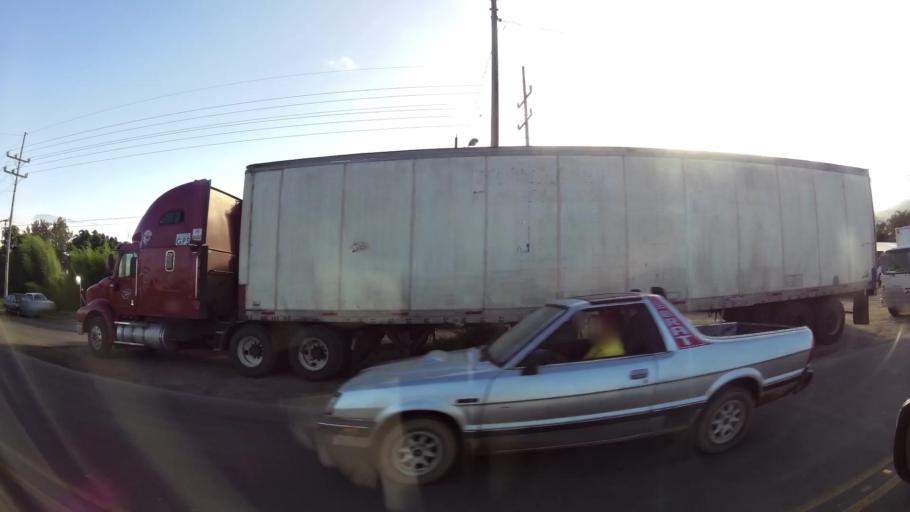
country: CR
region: Cartago
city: Tobosi
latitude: 9.8323
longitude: -83.9518
